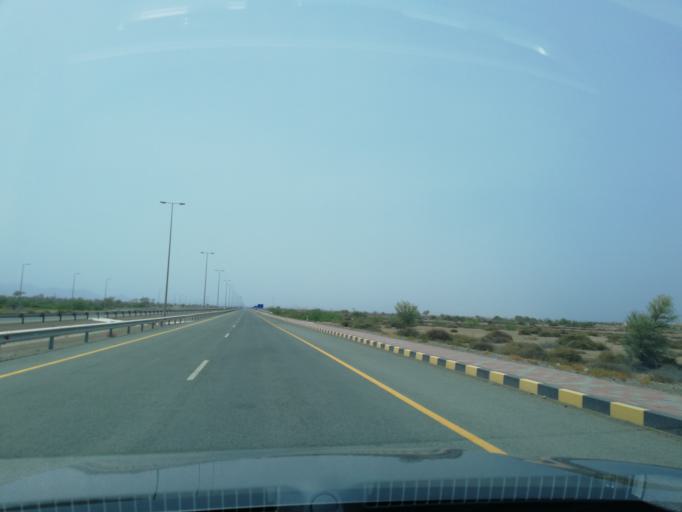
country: OM
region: Al Batinah
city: Shinas
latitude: 24.6632
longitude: 56.5066
